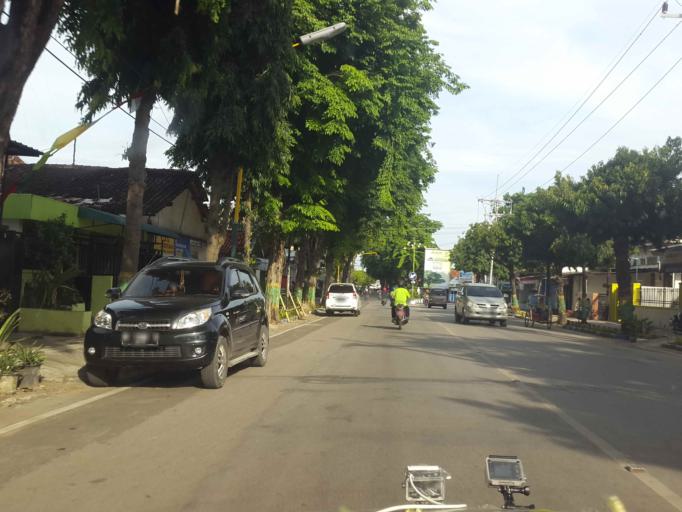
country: ID
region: East Java
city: Sumenep
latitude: -7.0070
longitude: 113.8632
